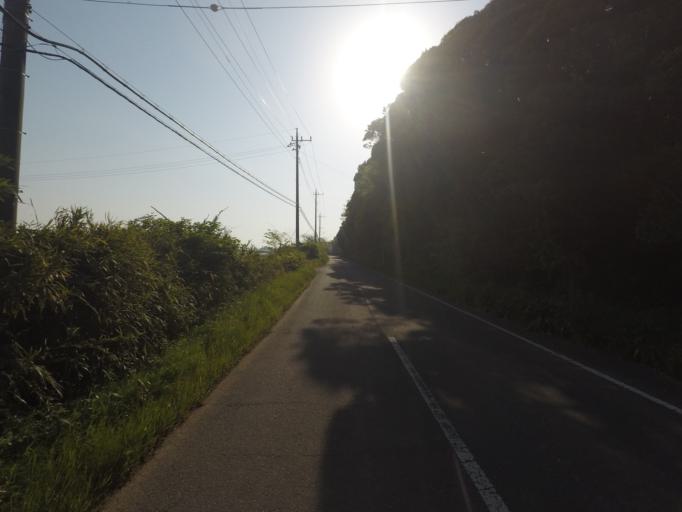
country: JP
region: Ibaraki
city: Inashiki
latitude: 36.0659
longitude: 140.3470
